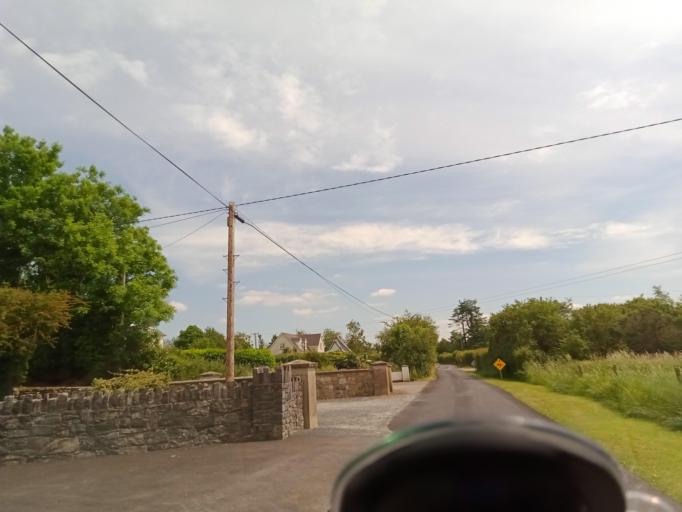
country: IE
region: Leinster
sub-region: Kilkenny
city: Thomastown
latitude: 52.5581
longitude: -7.1130
